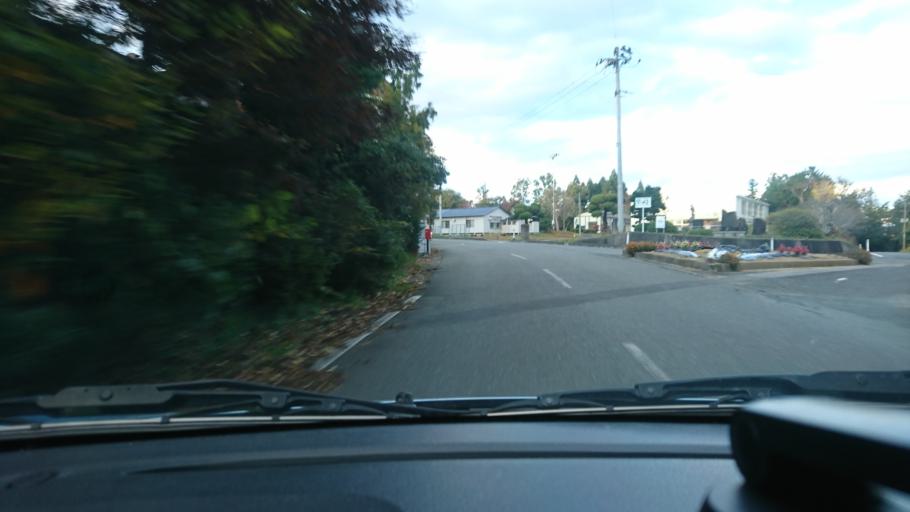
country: JP
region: Iwate
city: Ichinoseki
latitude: 38.7963
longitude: 141.1927
